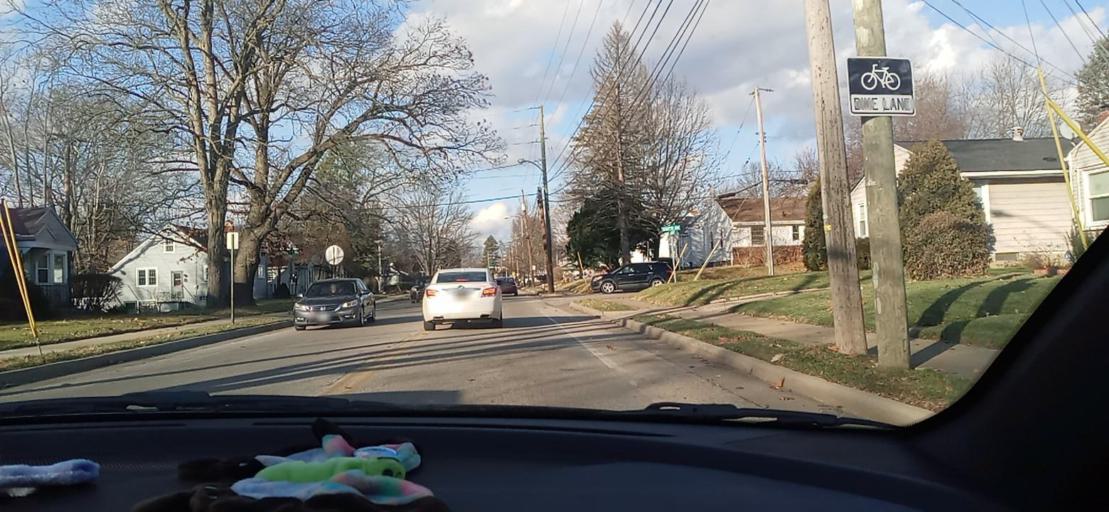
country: US
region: Ohio
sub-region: Summit County
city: Fairlawn
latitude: 41.1162
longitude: -81.5691
